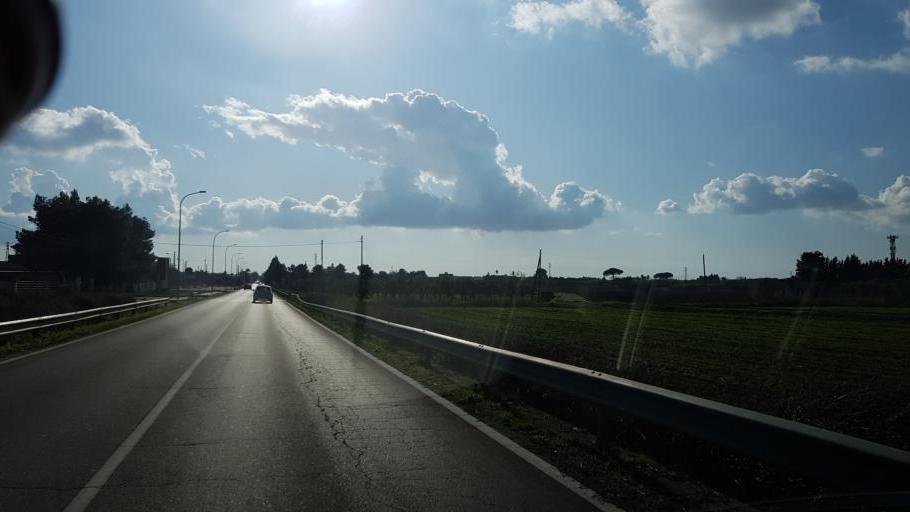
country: IT
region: Apulia
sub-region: Provincia di Lecce
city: Salice Salentino
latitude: 40.3973
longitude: 17.9702
